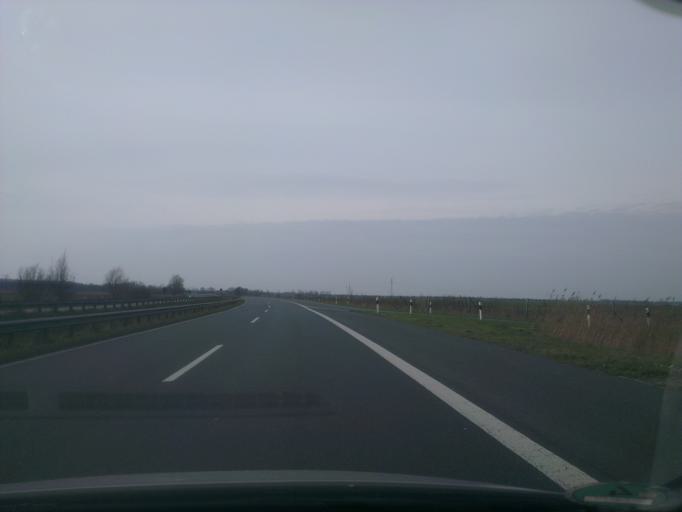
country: DE
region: Lower Saxony
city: Hinte
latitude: 53.3843
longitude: 7.1792
